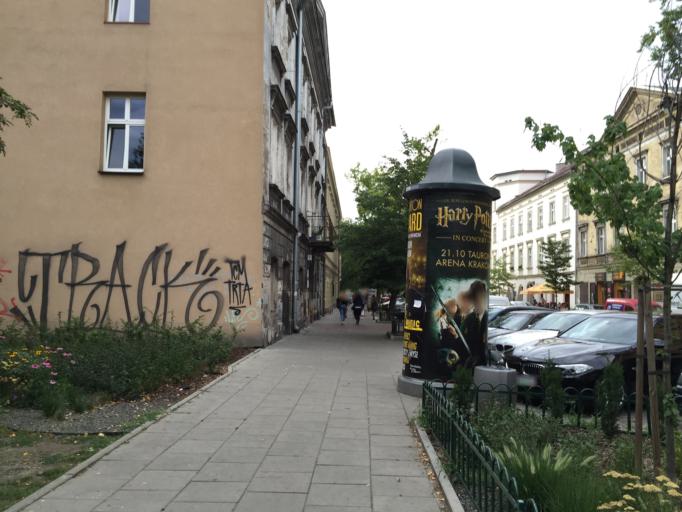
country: PL
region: Lesser Poland Voivodeship
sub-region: Krakow
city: Krakow
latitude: 50.0479
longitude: 19.9459
